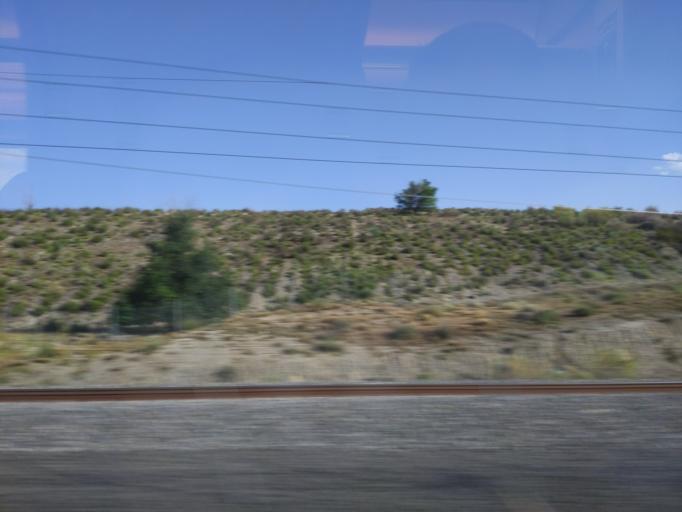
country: ES
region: Madrid
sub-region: Provincia de Madrid
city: Villa de Vallecas
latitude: 40.3356
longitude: -3.6288
